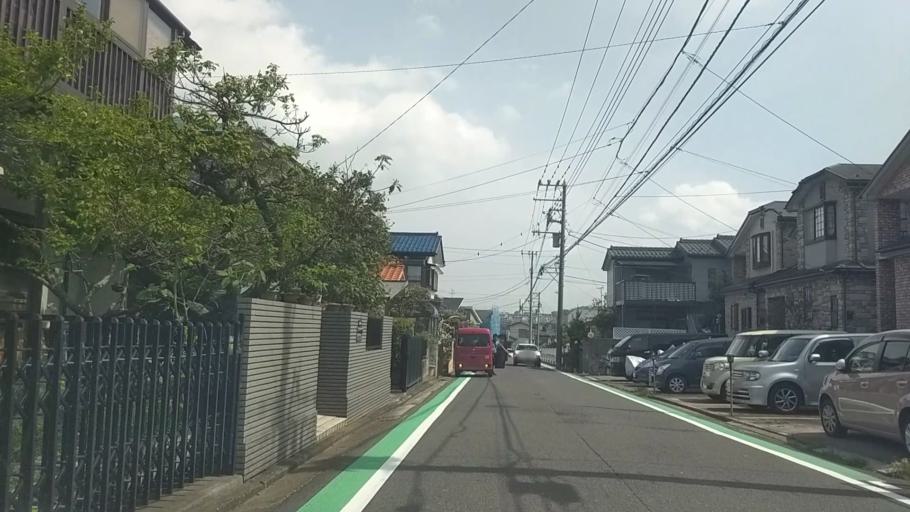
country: JP
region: Kanagawa
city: Yokohama
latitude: 35.3907
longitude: 139.5926
